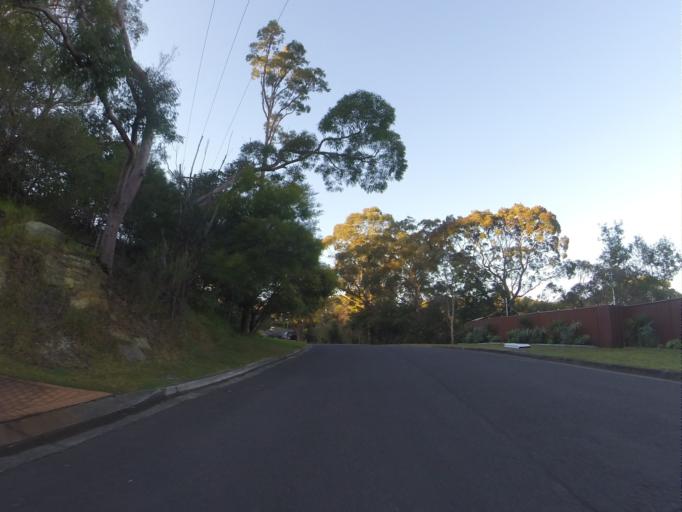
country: AU
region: New South Wales
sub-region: Sutherland Shire
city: Engadine
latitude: -34.0731
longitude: 151.0070
